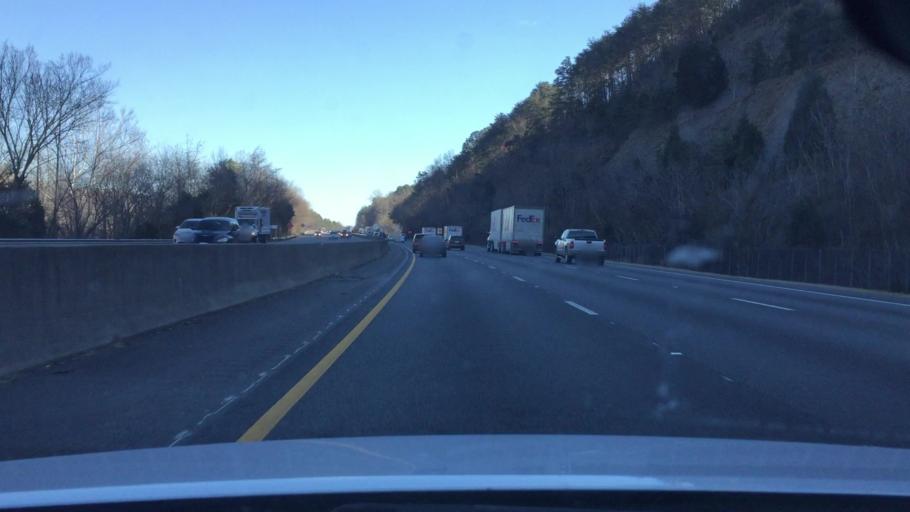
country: US
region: Georgia
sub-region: Catoosa County
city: Ringgold
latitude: 34.9066
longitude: -85.1015
